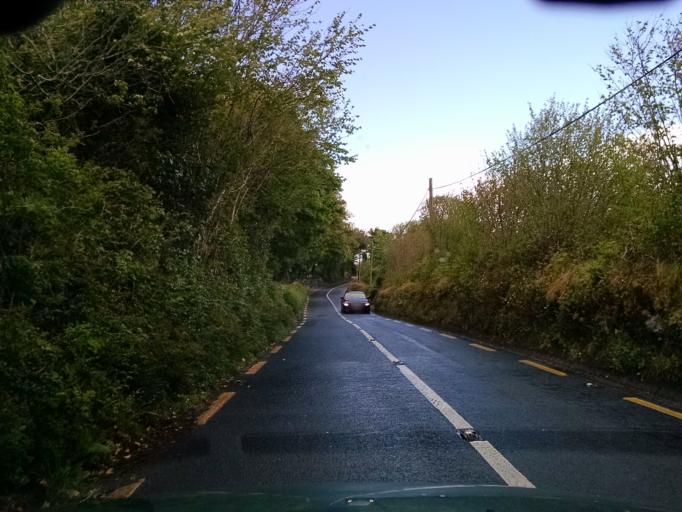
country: IE
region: Connaught
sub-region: County Galway
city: Bearna
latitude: 53.0893
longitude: -9.1737
